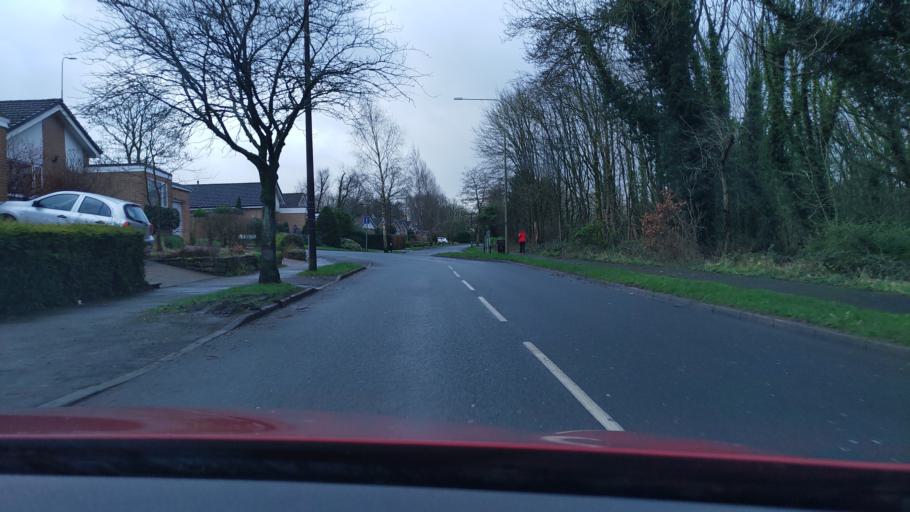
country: GB
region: England
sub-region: Lancashire
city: Coppull
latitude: 53.6509
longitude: -2.6508
